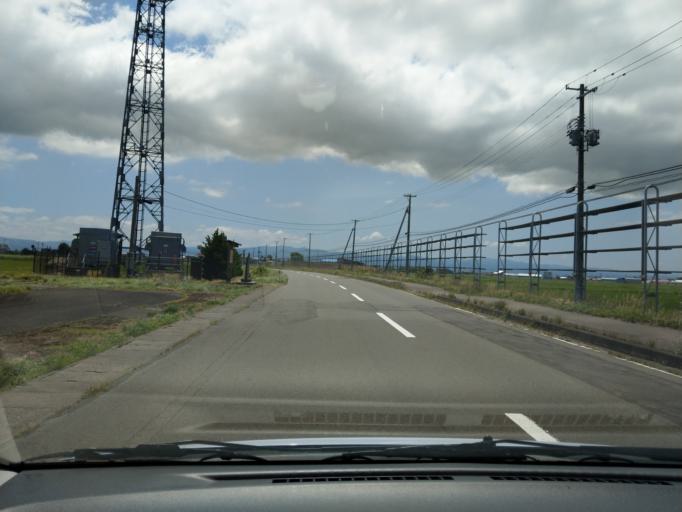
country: JP
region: Aomori
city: Kuroishi
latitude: 40.6740
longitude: 140.5579
